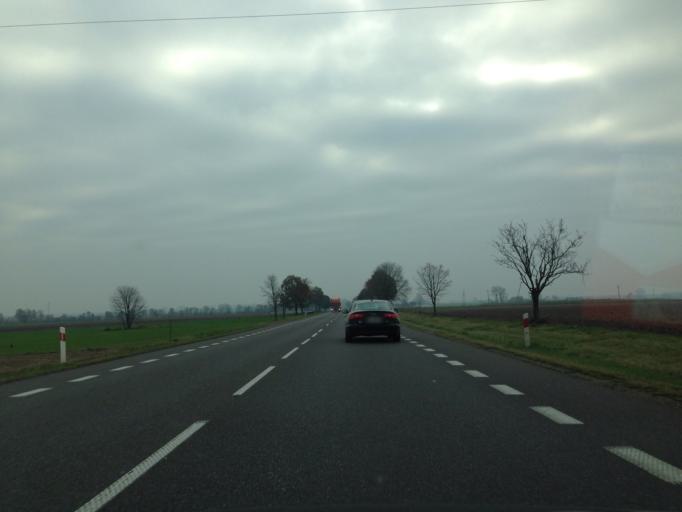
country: PL
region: Masovian Voivodeship
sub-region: Powiat plocki
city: Drobin
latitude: 52.7317
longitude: 20.0021
